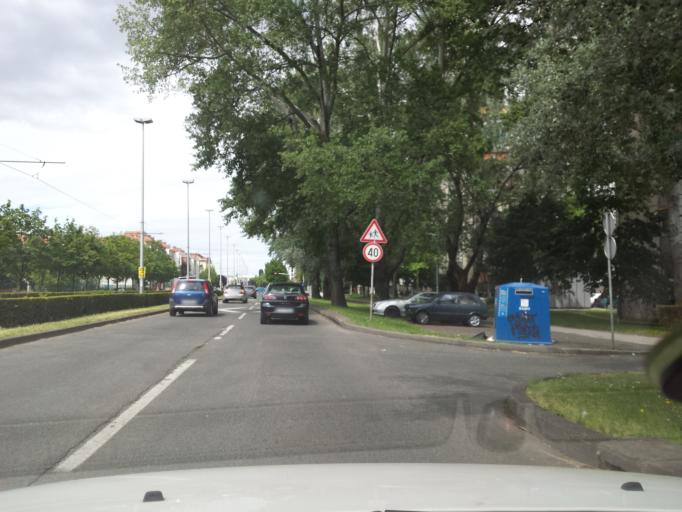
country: HR
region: Grad Zagreb
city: Novi Zagreb
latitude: 45.7883
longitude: 15.9437
